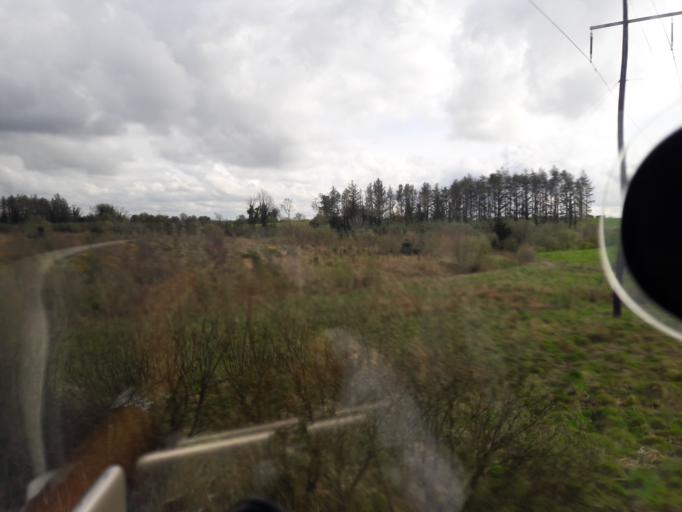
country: IE
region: Leinster
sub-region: An Iarmhi
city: An Muileann gCearr
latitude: 53.5027
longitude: -7.2715
